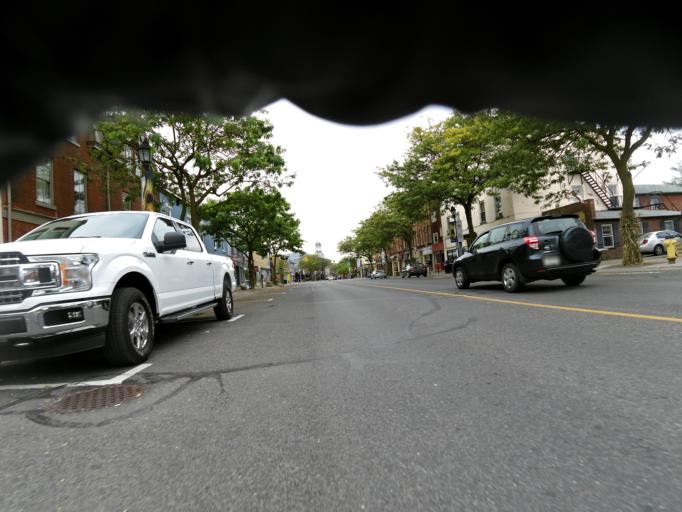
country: CA
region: Ontario
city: Cobourg
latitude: 43.9602
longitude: -78.1645
